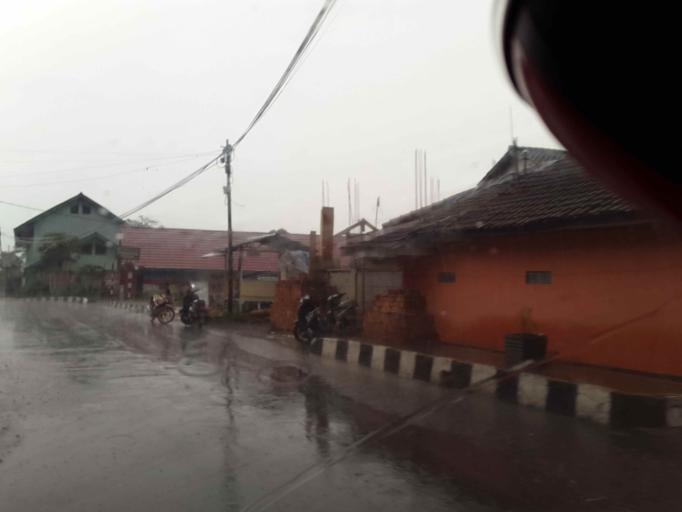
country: ID
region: West Java
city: Sukabumi
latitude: -6.9066
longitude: 106.9175
